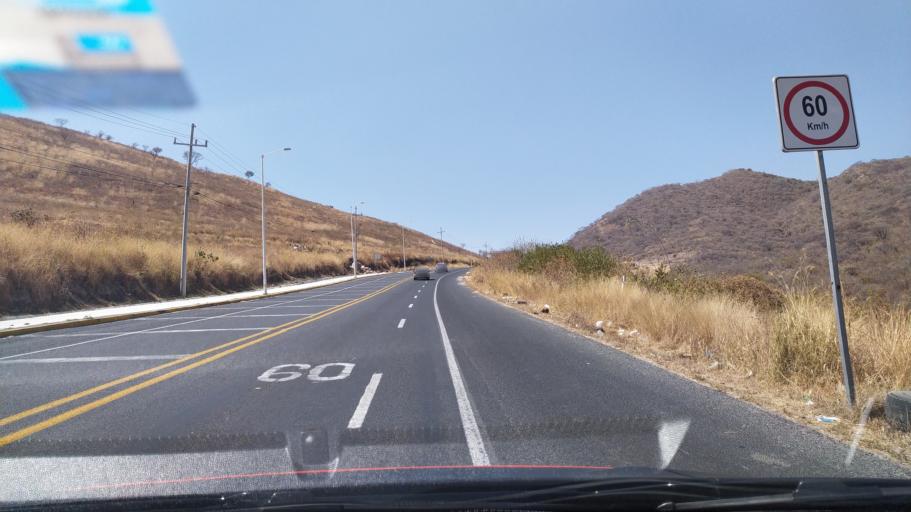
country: MX
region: Jalisco
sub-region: Tlajomulco de Zuniga
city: Lomas del Sur
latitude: 20.4884
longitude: -103.4213
